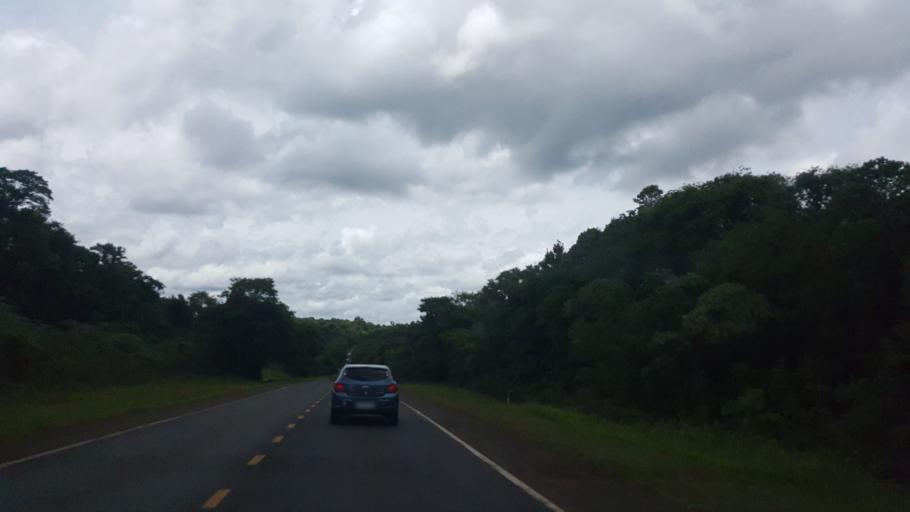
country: AR
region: Misiones
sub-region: Departamento de Iguazu
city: Puerto Iguazu
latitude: -25.6838
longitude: -54.5103
